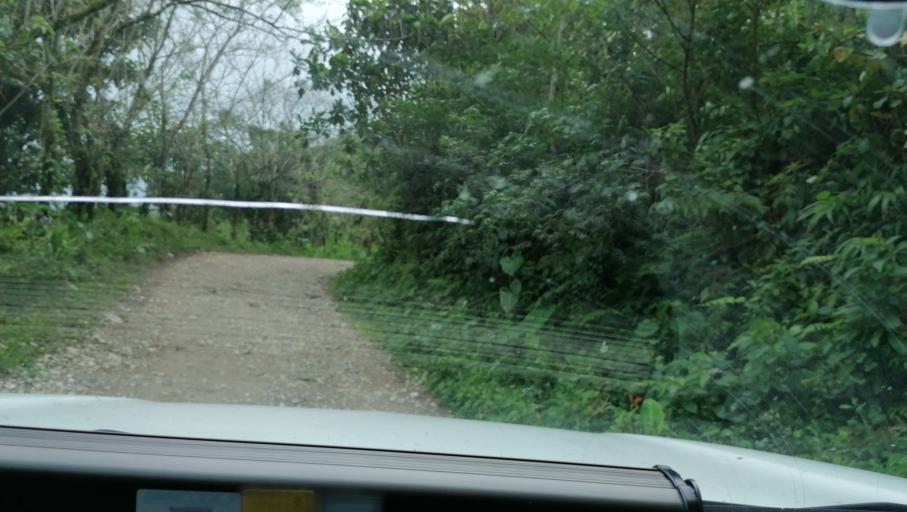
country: MX
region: Chiapas
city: Ixtacomitan
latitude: 17.3528
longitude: -93.1454
